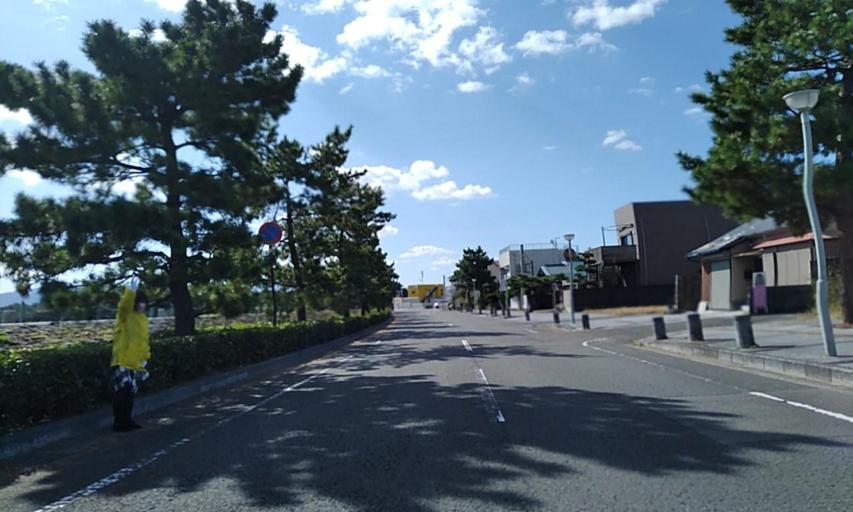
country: JP
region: Wakayama
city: Minato
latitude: 34.1851
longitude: 135.1722
